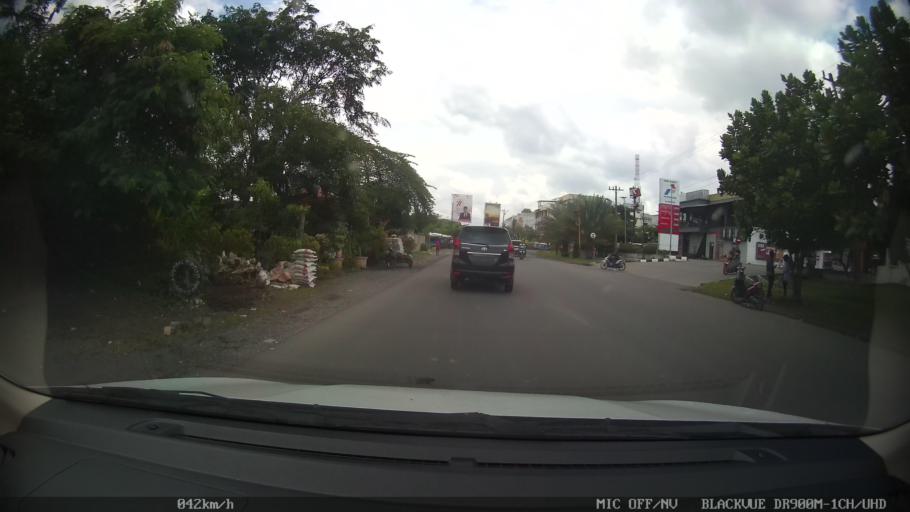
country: ID
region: North Sumatra
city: Medan
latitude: 3.6296
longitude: 98.7079
